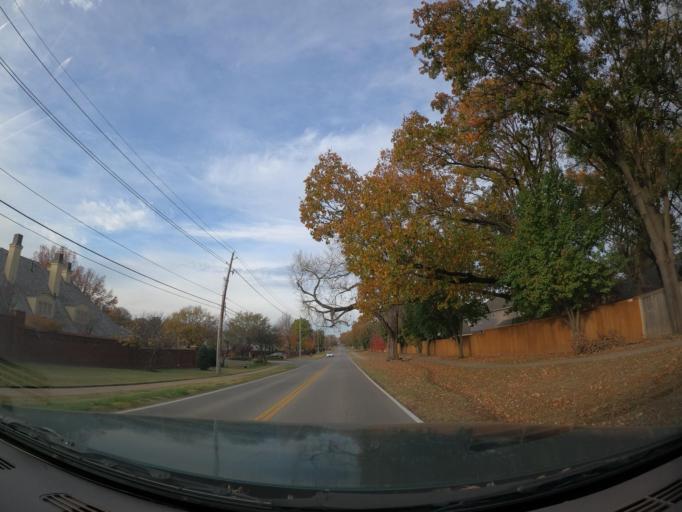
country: US
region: Oklahoma
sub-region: Tulsa County
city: Jenks
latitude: 36.0366
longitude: -95.9400
